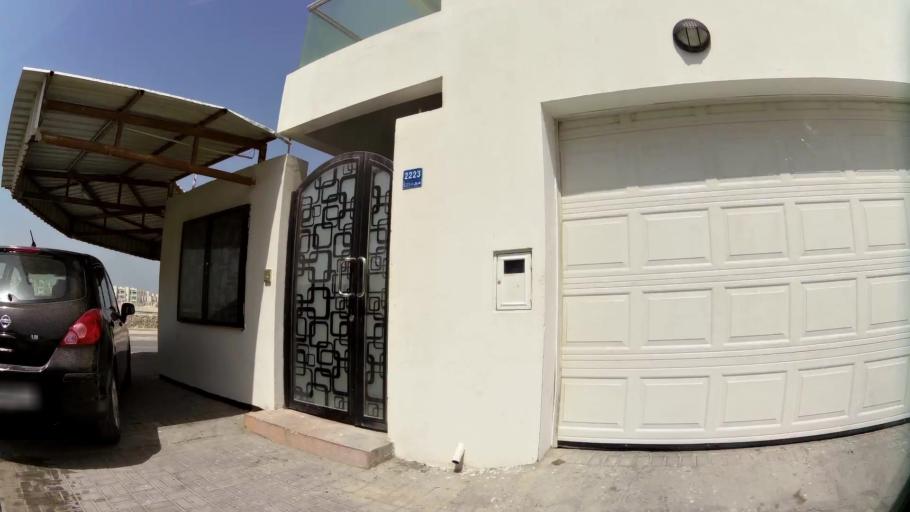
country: BH
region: Manama
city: Jidd Hafs
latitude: 26.2181
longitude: 50.4467
